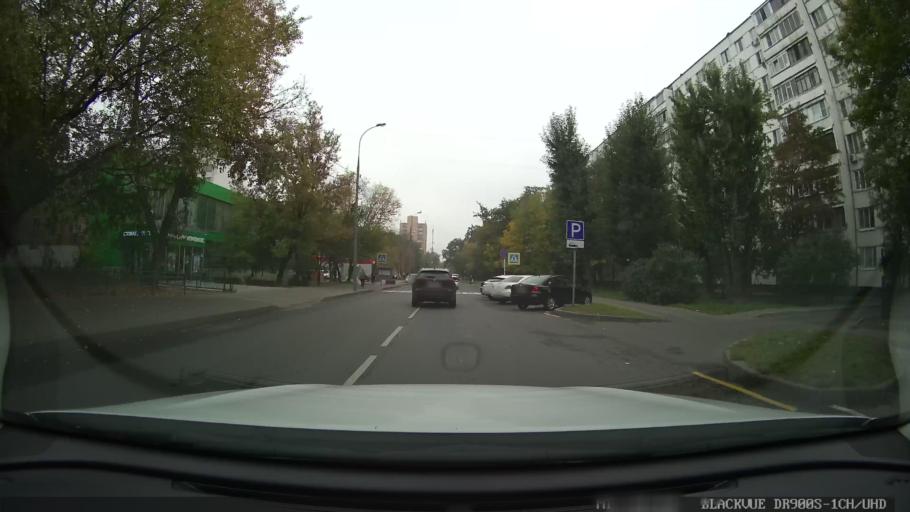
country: RU
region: Moscow
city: Kolomenskoye
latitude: 55.6859
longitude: 37.6837
